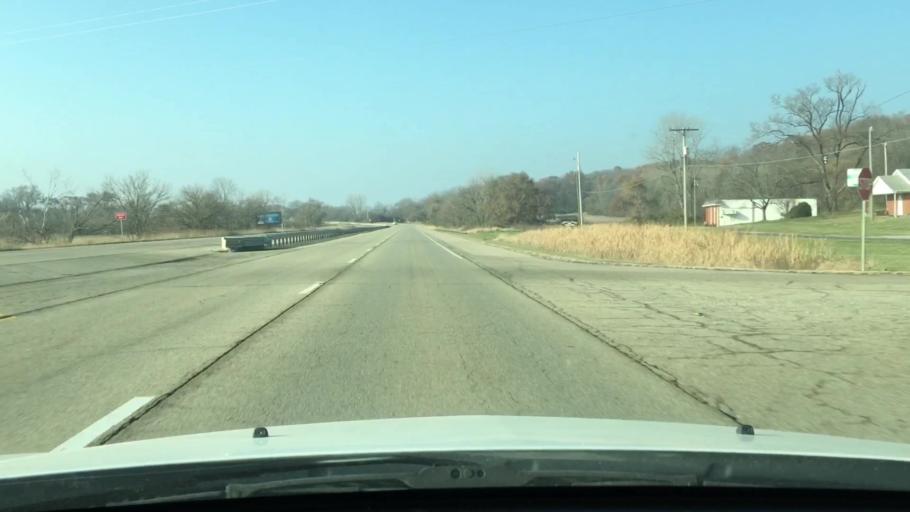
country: US
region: Illinois
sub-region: Tazewell County
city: Pekin
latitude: 40.5757
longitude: -89.7086
